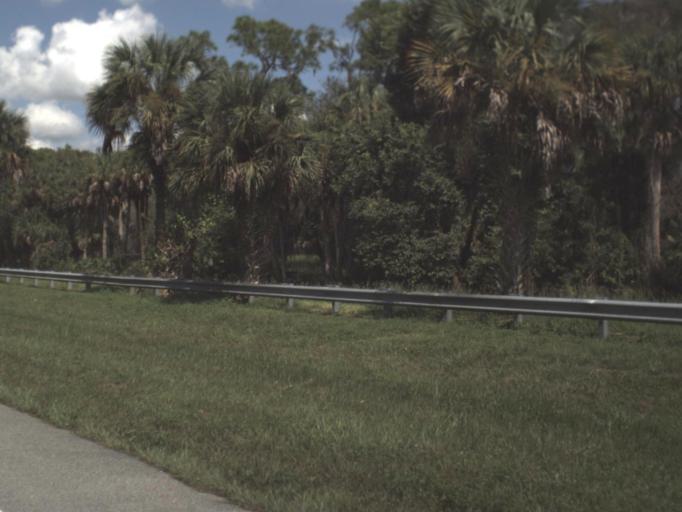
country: US
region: Florida
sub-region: Collier County
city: Immokalee
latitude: 26.2728
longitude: -81.3422
